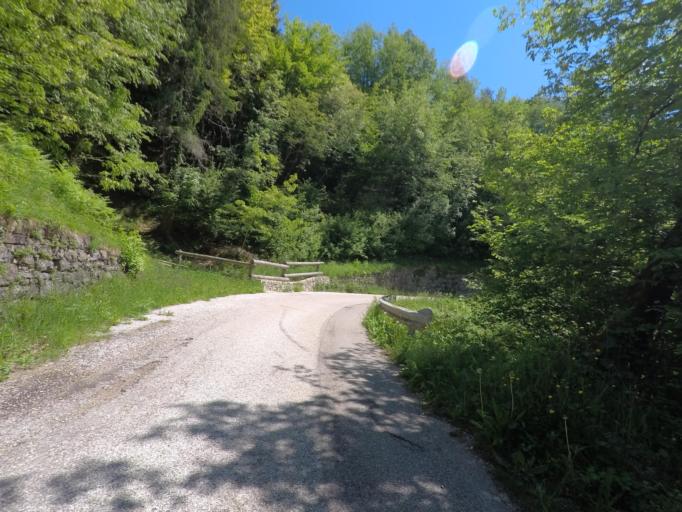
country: IT
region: Friuli Venezia Giulia
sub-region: Provincia di Udine
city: Raveo
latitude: 46.4412
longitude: 12.8829
